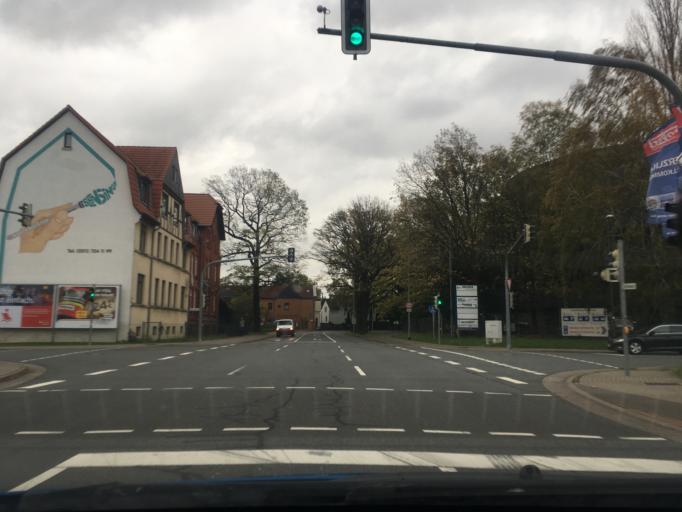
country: DE
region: Lower Saxony
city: Langenhagen
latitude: 52.4543
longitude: 9.7337
